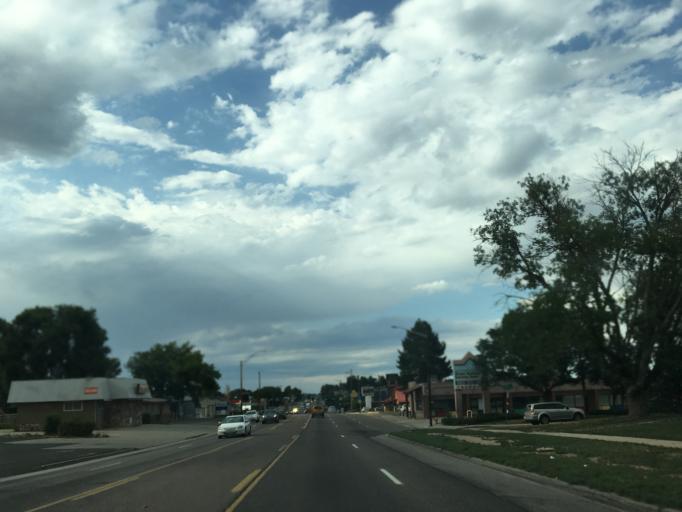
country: US
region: Colorado
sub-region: Jefferson County
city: Lakewood
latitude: 39.7161
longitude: -105.0533
